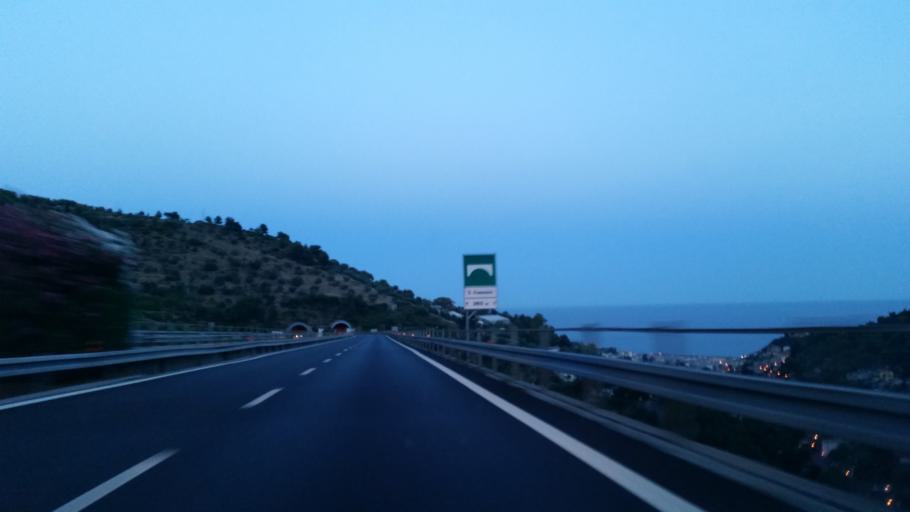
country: IT
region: Liguria
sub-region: Provincia di Imperia
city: San Remo
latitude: 43.8376
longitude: 7.7602
